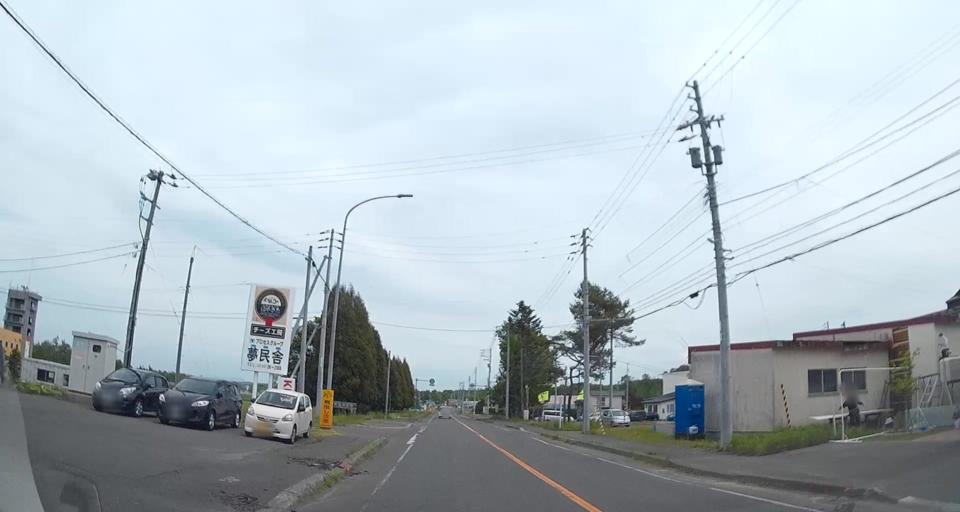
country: JP
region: Hokkaido
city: Chitose
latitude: 42.7692
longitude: 141.8244
